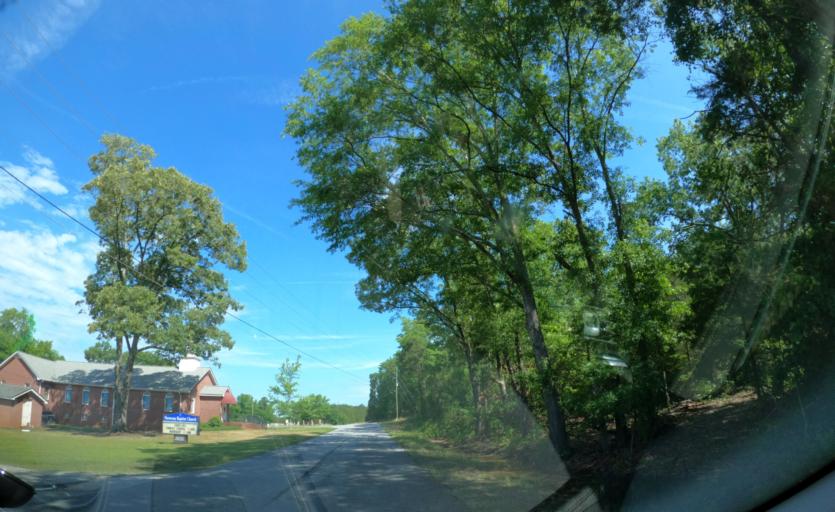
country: US
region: Georgia
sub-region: Elbert County
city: Elberton
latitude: 34.1793
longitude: -82.8540
